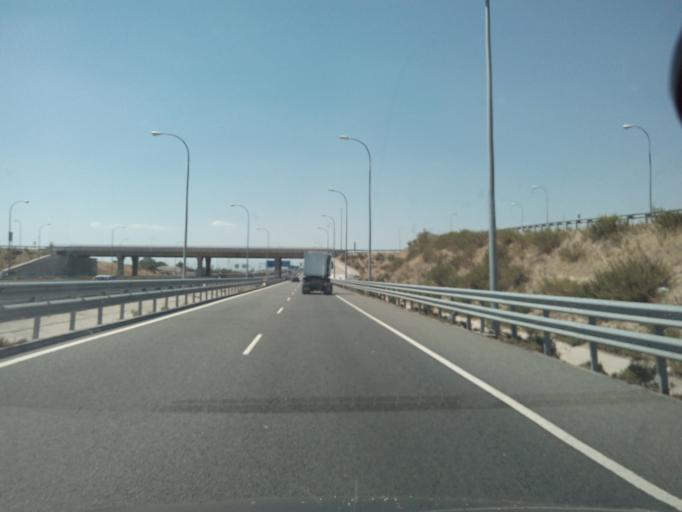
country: ES
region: Madrid
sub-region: Provincia de Madrid
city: San Fernando de Henares
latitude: 40.4339
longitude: -3.5042
